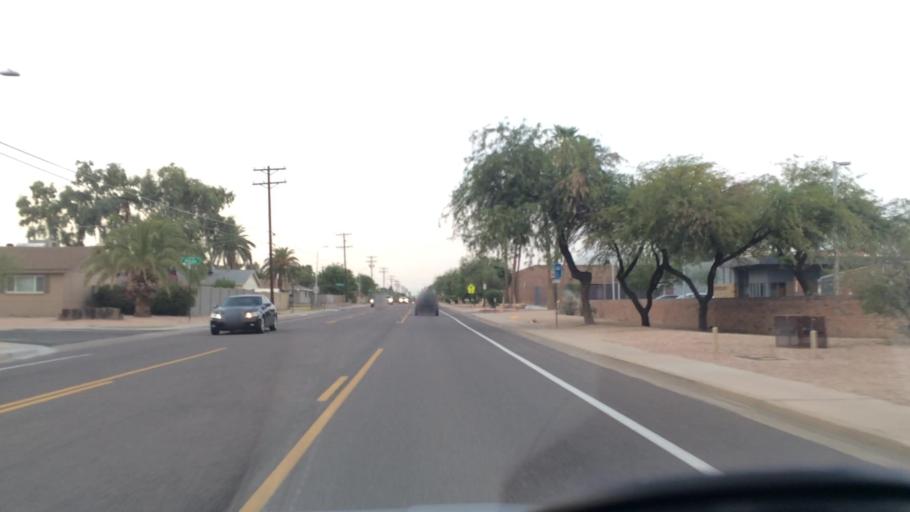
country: US
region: Arizona
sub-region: Maricopa County
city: Tempe
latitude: 33.4547
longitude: -111.9178
